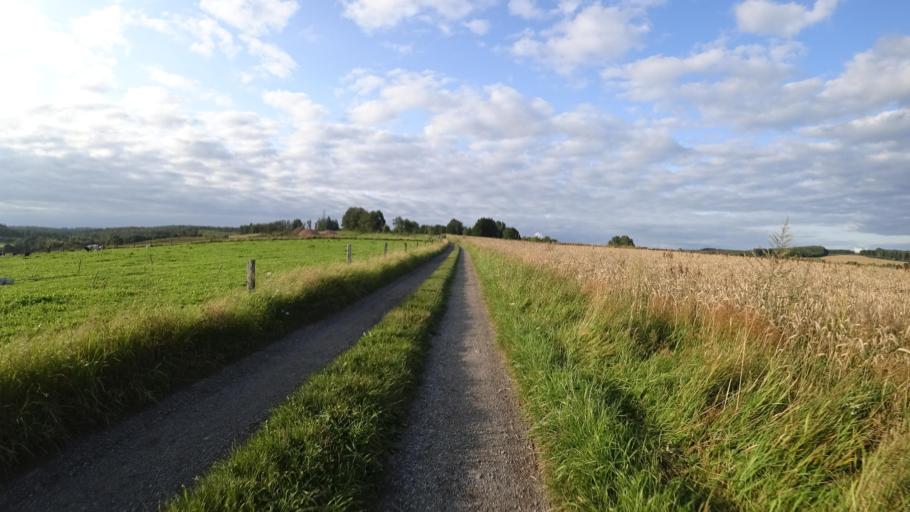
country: BE
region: Wallonia
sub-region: Province du Luxembourg
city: Neufchateau
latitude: 49.8610
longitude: 5.3699
